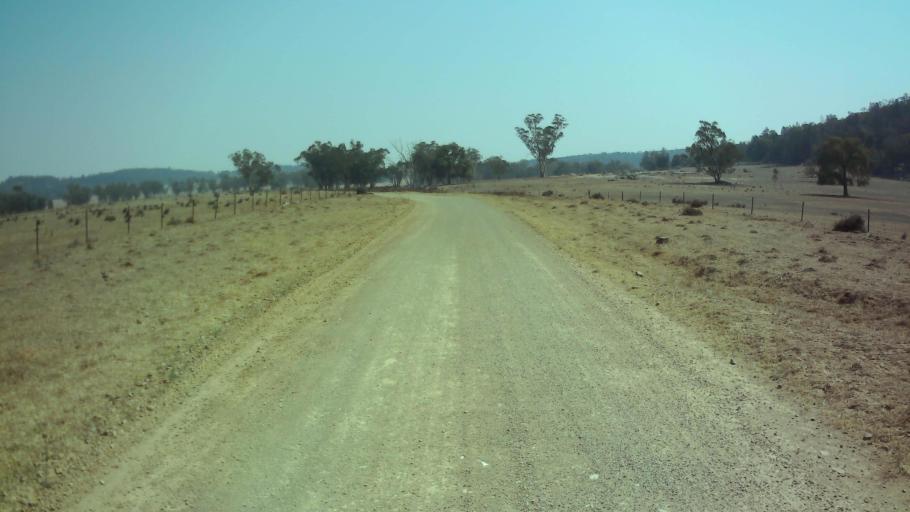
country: AU
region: New South Wales
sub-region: Weddin
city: Grenfell
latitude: -33.6788
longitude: 148.2770
